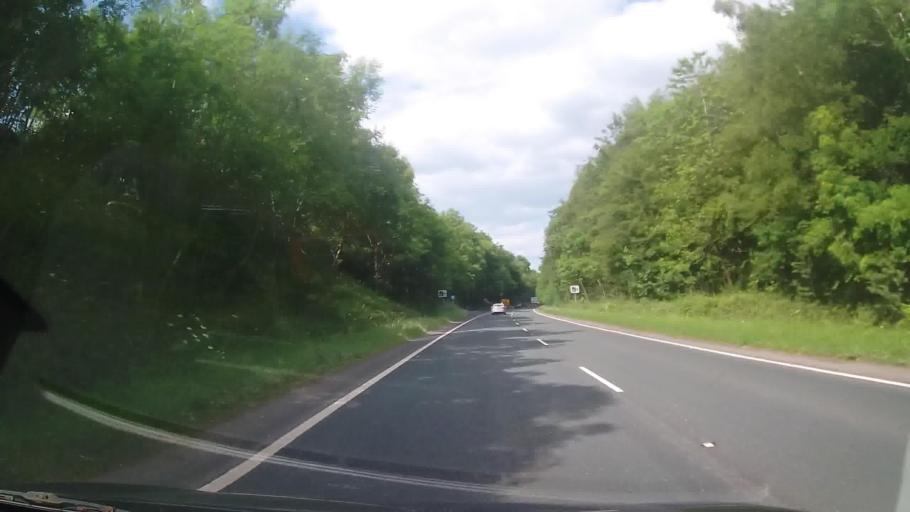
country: GB
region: England
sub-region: Shropshire
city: Ludlow
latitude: 52.3509
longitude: -2.7075
